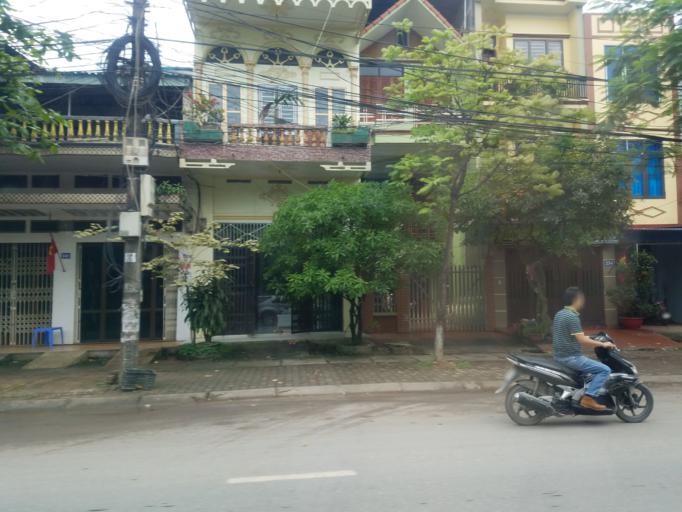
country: VN
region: Thai Nguyen
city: Thanh Pho Thai Nguyen
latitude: 21.5781
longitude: 105.8356
